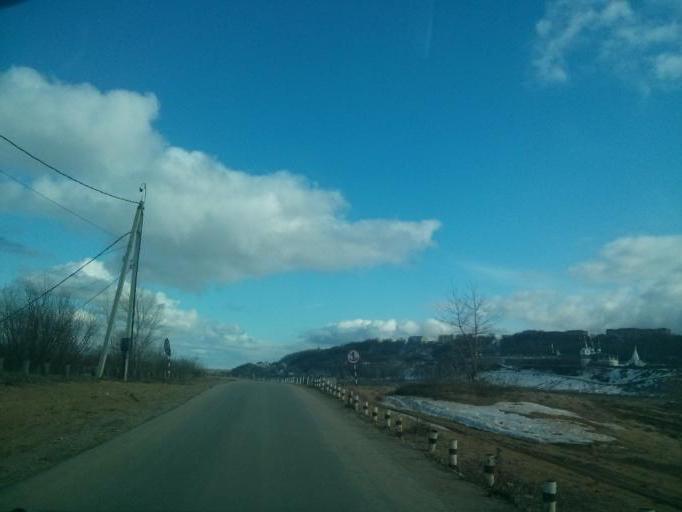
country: RU
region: Nizjnij Novgorod
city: Nizhniy Novgorod
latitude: 56.3294
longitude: 44.0439
